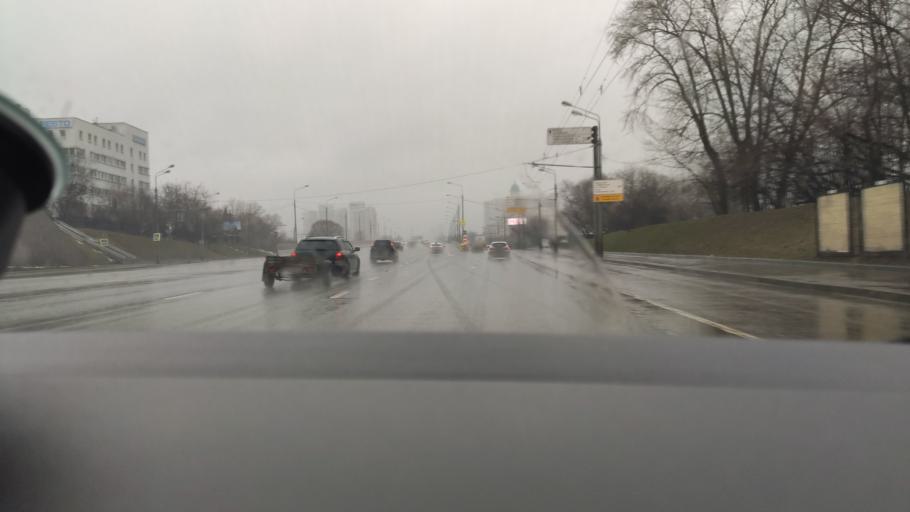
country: RU
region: Moscow
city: Nikol'skoye
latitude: 55.6891
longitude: 37.4807
